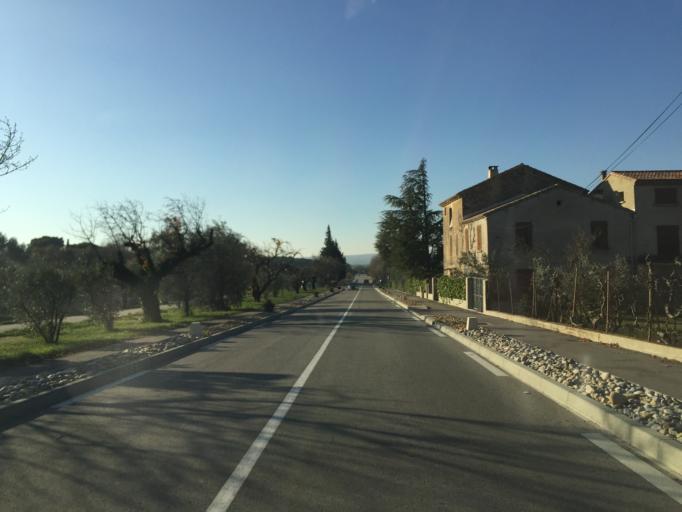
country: FR
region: Provence-Alpes-Cote d'Azur
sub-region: Departement du Vaucluse
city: Sainte-Cecile-les-Vignes
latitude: 44.2300
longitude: 4.9259
